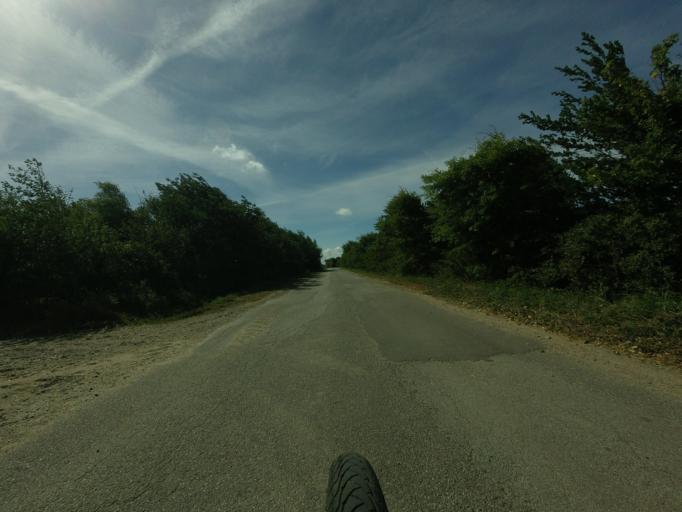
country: DK
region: North Denmark
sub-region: Hjorring Kommune
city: Vra
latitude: 57.3351
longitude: 9.8098
